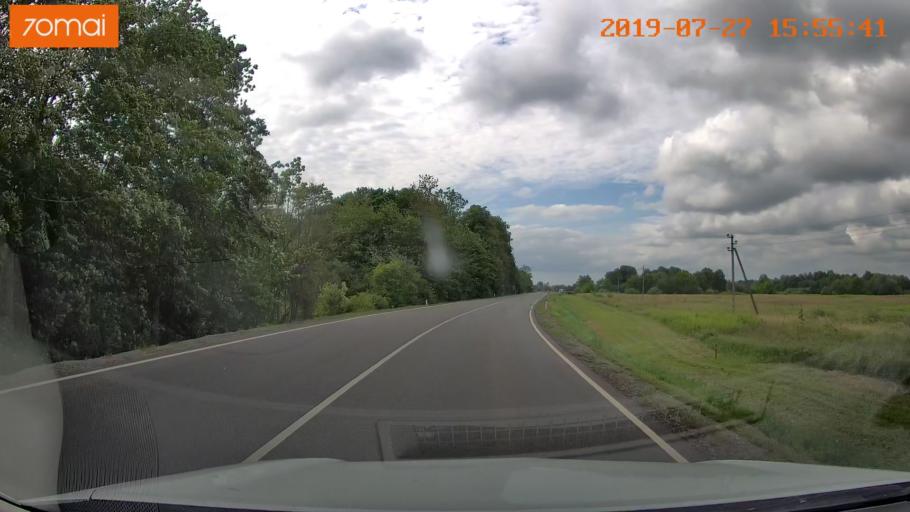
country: RU
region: Kaliningrad
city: Chernyakhovsk
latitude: 54.6145
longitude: 21.9159
